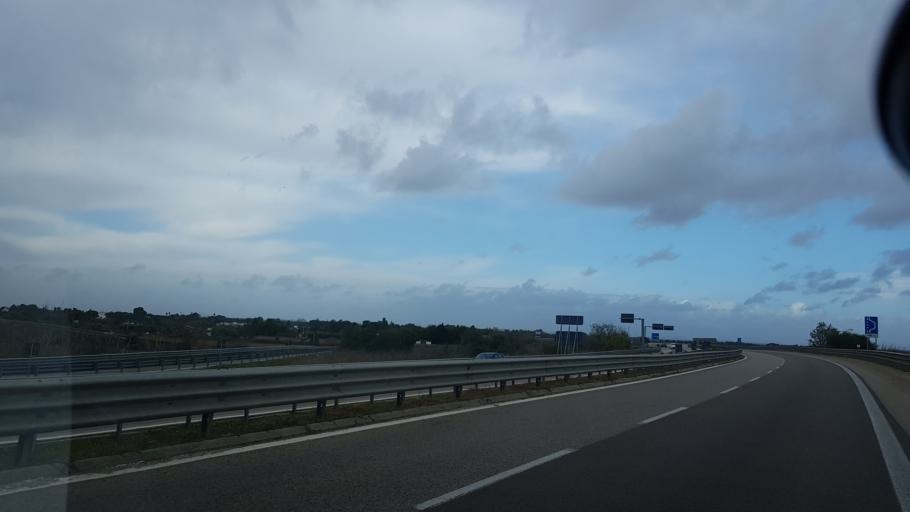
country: IT
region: Apulia
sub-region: Provincia di Brindisi
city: Mesagne
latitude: 40.5705
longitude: 17.8147
